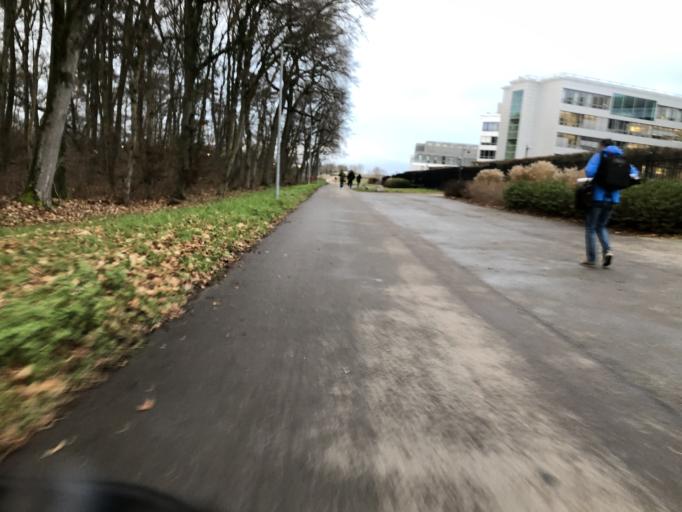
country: DE
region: Baden-Wuerttemberg
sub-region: Karlsruhe Region
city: Walldorf
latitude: 49.2931
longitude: 8.6369
